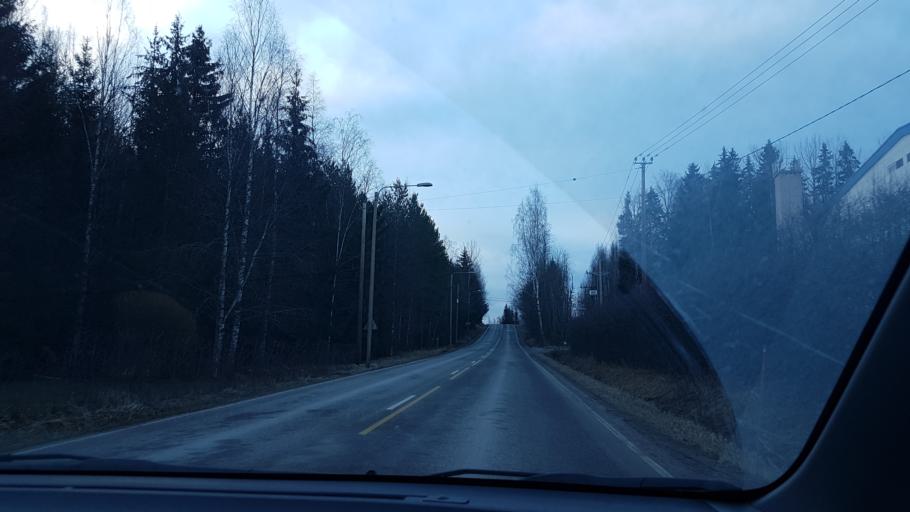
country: FI
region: Uusimaa
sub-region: Helsinki
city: Nurmijaervi
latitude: 60.3588
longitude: 24.7446
